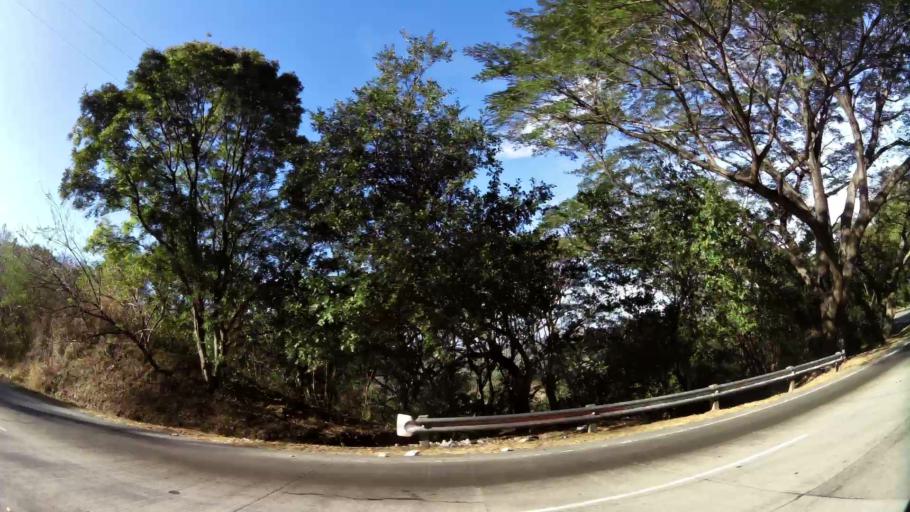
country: SV
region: Santa Ana
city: Santa Ana
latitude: 14.0552
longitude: -89.5109
